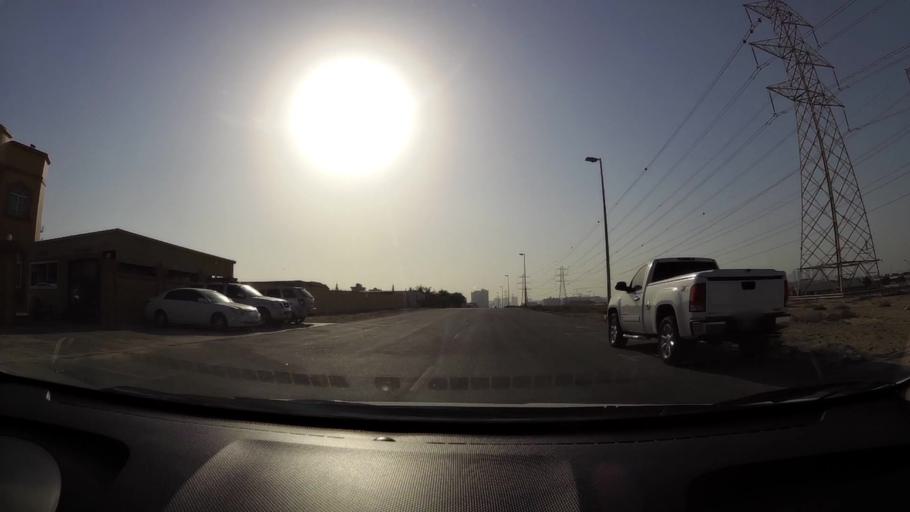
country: AE
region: Ash Shariqah
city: Sharjah
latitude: 25.2700
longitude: 55.3935
